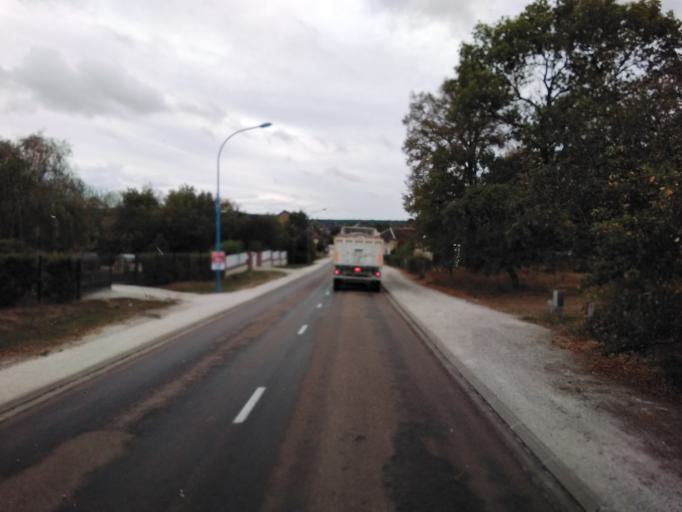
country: FR
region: Champagne-Ardenne
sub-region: Departement de l'Aube
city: Vendeuvre-sur-Barse
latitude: 48.2999
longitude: 4.5179
